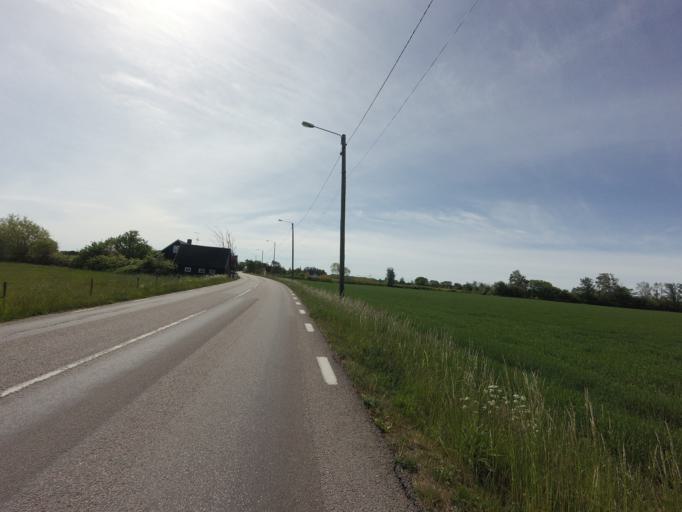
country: SE
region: Skane
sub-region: Helsingborg
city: Odakra
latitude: 56.1478
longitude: 12.6787
